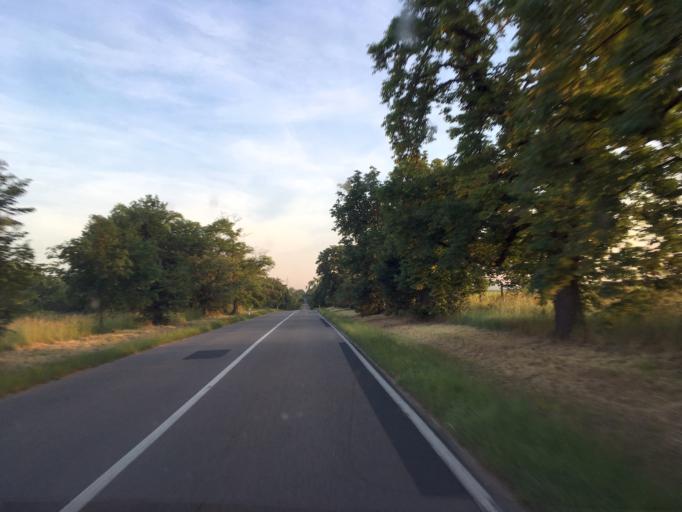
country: CZ
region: South Moravian
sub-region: Okres Breclav
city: Hlohovec
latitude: 48.7663
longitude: 16.7766
